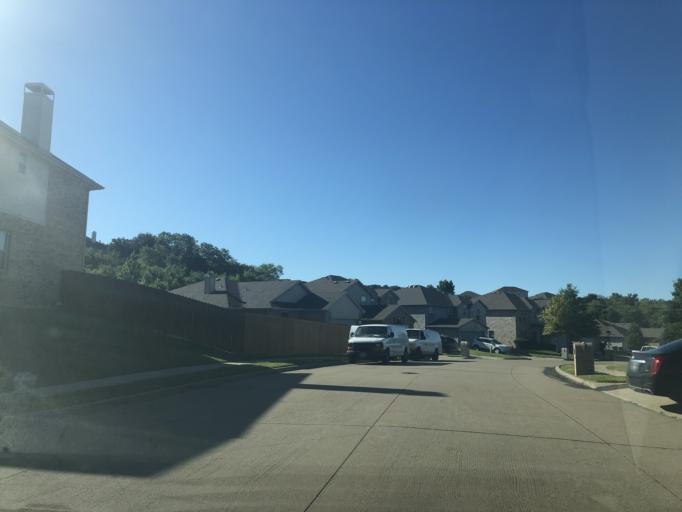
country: US
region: Texas
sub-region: Dallas County
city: Cedar Hill
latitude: 32.6452
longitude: -96.9719
